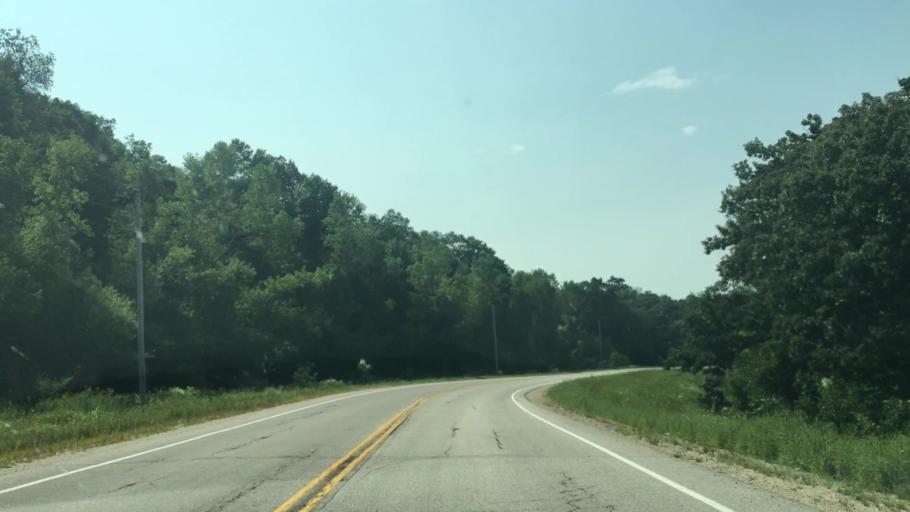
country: US
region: Minnesota
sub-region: Fillmore County
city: Preston
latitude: 43.7007
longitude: -91.9673
